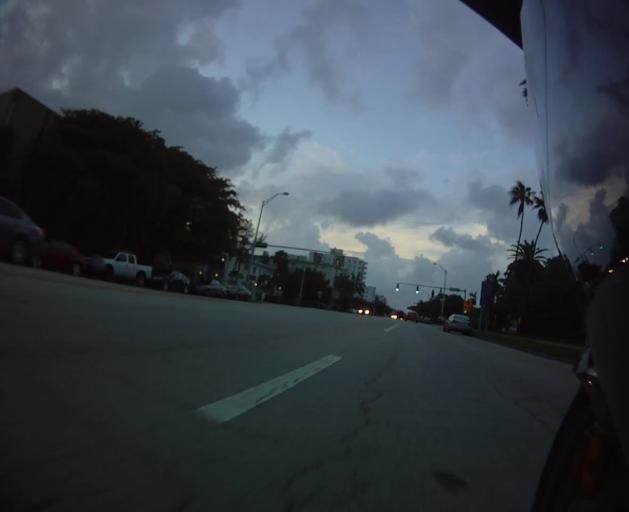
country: US
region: Florida
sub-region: Miami-Dade County
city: Miami Beach
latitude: 25.7822
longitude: -80.1409
